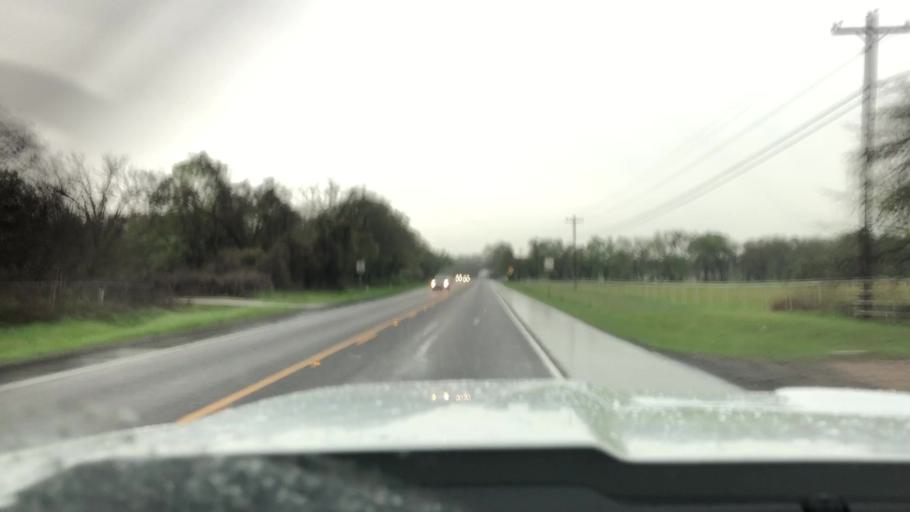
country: US
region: Texas
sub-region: Johnson County
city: Keene
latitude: 32.4319
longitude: -97.3142
